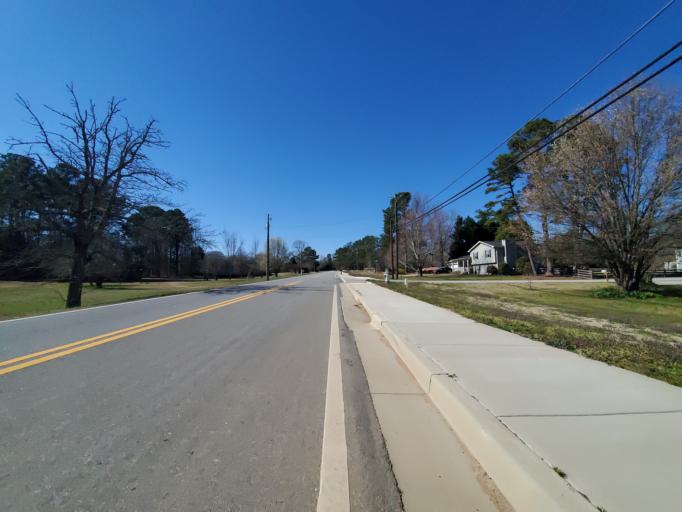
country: US
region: Georgia
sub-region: Gwinnett County
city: Dacula
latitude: 33.9800
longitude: -83.8787
